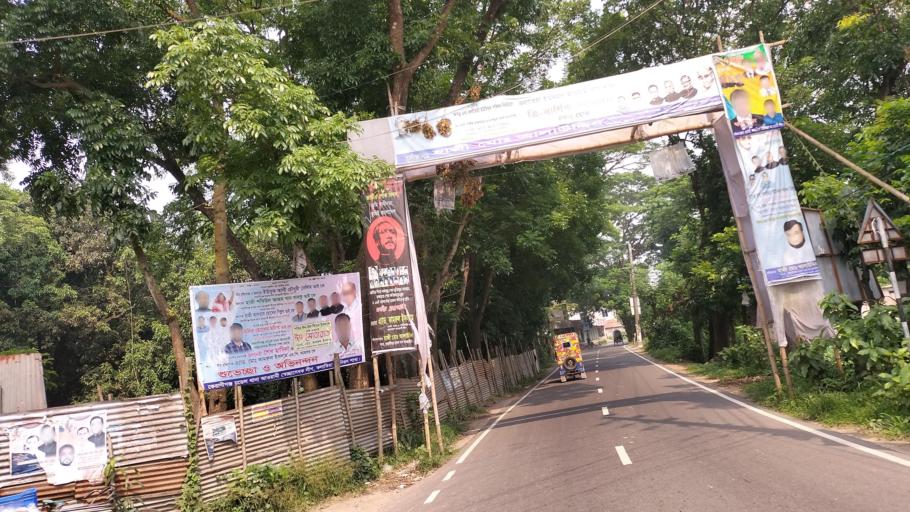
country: BD
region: Dhaka
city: Azimpur
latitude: 23.6959
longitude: 90.2984
